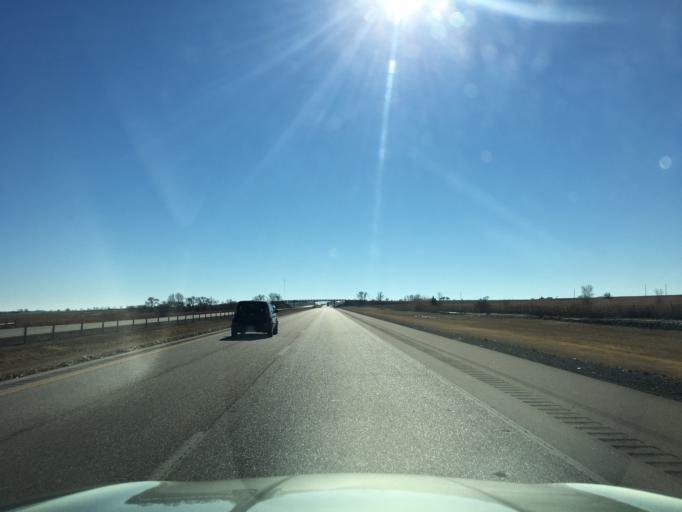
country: US
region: Oklahoma
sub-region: Kay County
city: Blackwell
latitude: 36.8884
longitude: -97.3529
